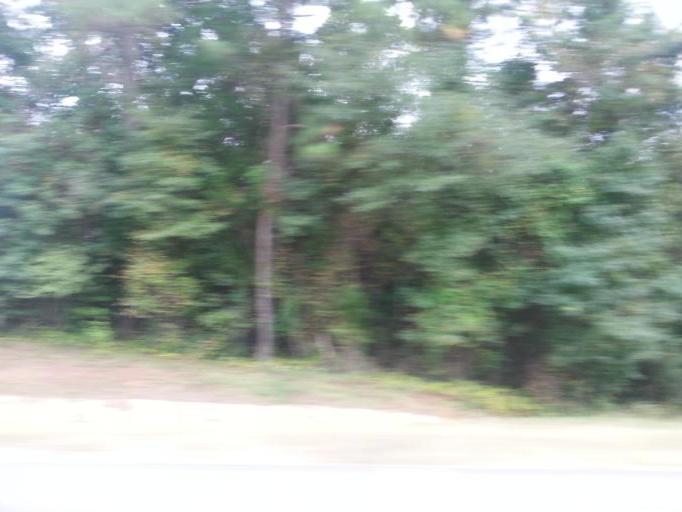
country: US
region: Alabama
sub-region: Conecuh County
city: Evergreen
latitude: 31.4708
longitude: -86.9541
